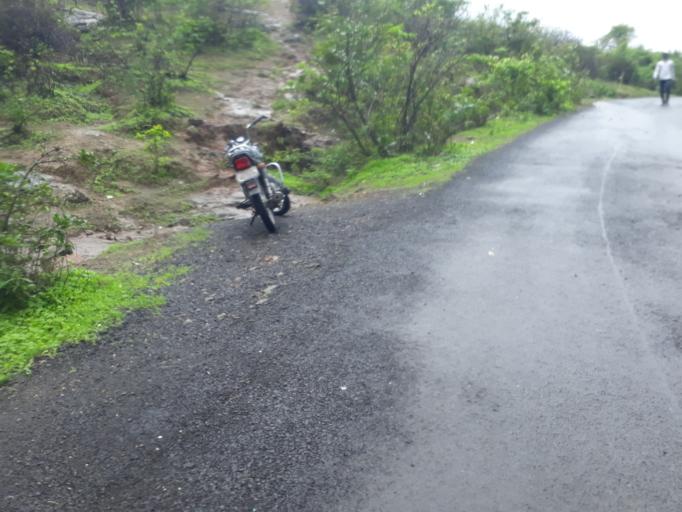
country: IN
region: Maharashtra
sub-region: Pune Division
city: Lonavla
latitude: 18.7247
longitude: 73.4772
